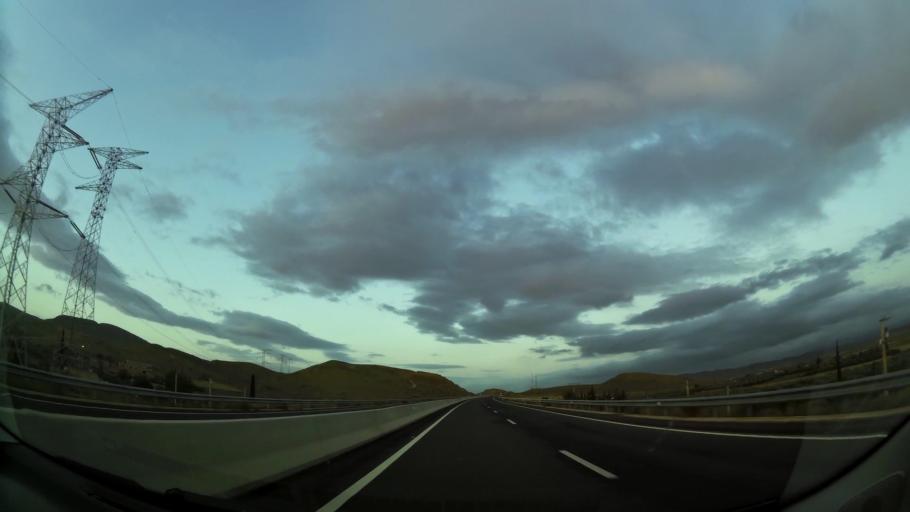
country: MA
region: Oriental
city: El Aioun
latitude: 34.5949
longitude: -2.6751
